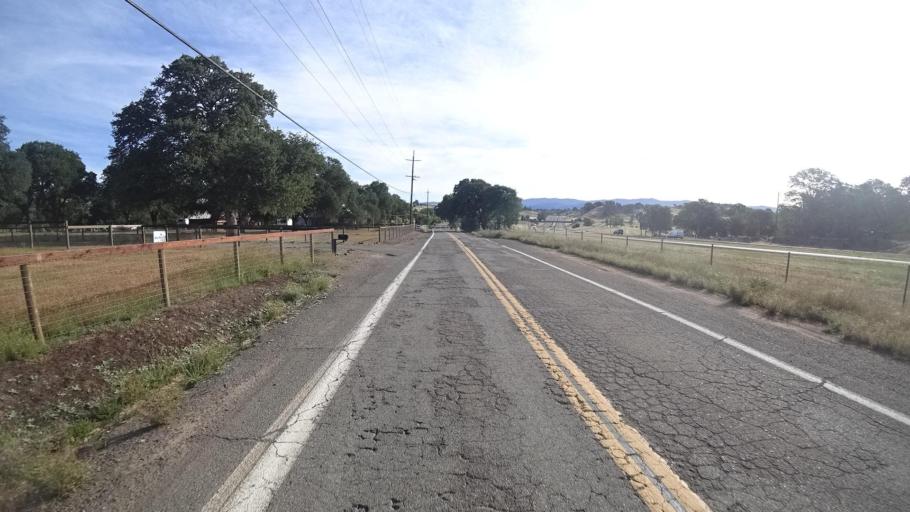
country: US
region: California
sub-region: Lake County
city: North Lakeport
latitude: 39.0814
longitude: -122.9302
